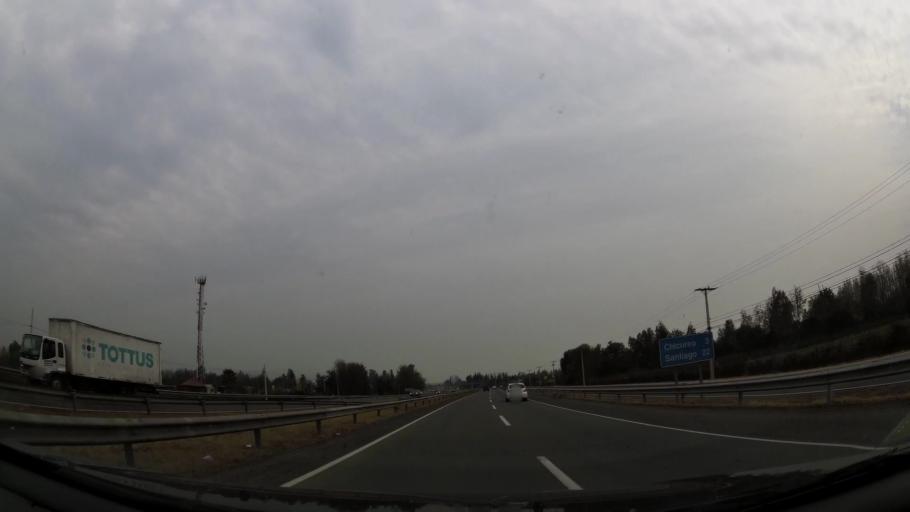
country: CL
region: Santiago Metropolitan
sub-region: Provincia de Chacabuco
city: Chicureo Abajo
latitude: -33.2569
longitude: -70.6980
